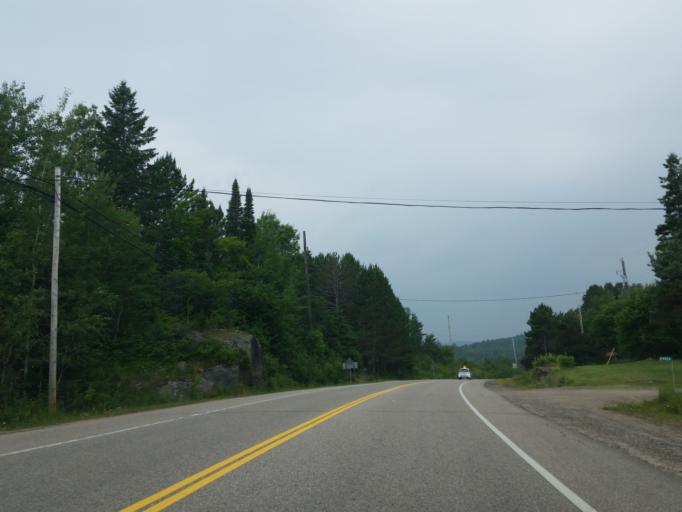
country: CA
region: Ontario
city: Bancroft
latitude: 45.4895
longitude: -78.2322
